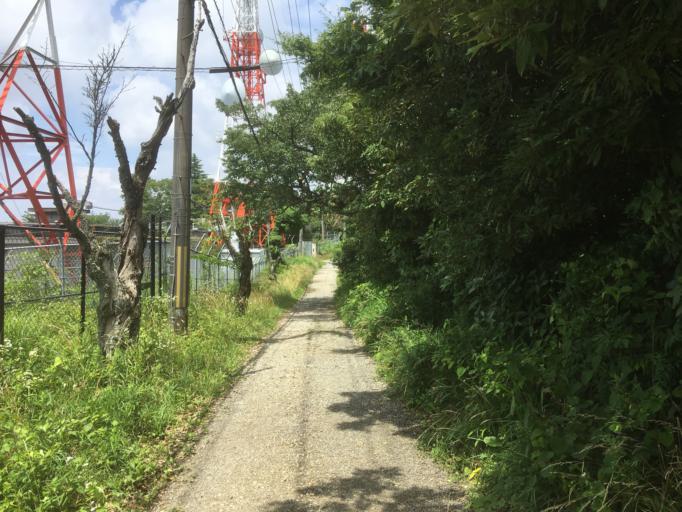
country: JP
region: Nara
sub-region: Ikoma-shi
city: Ikoma
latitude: 34.6752
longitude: 135.6770
